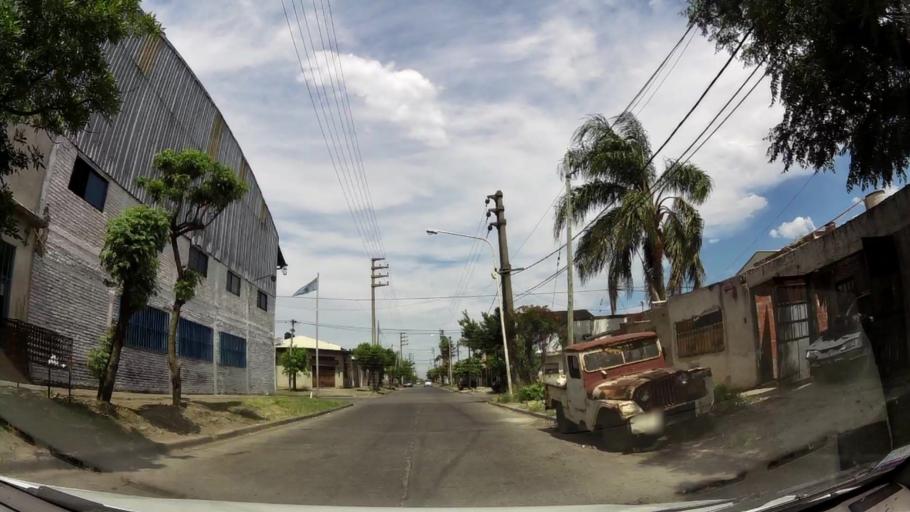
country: AR
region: Buenos Aires
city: San Justo
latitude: -34.6902
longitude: -58.5482
